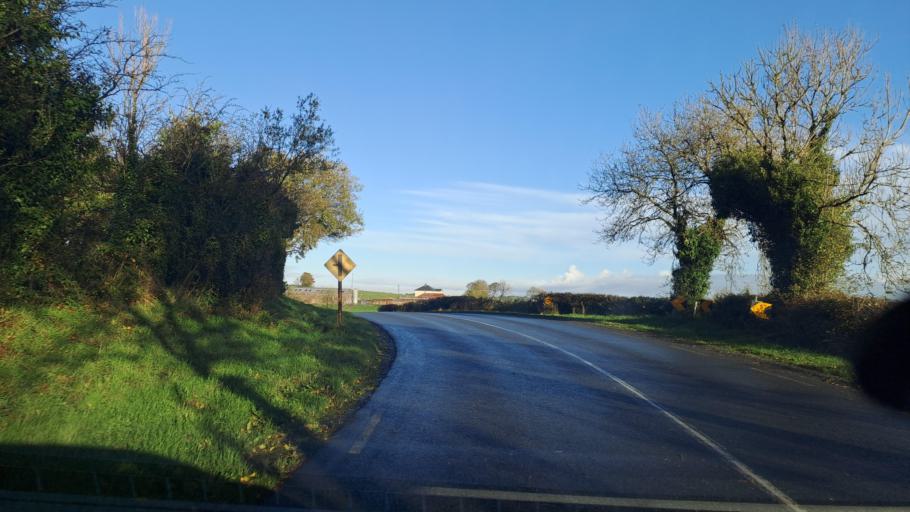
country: IE
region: Ulster
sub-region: County Monaghan
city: Monaghan
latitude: 54.1568
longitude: -7.0032
